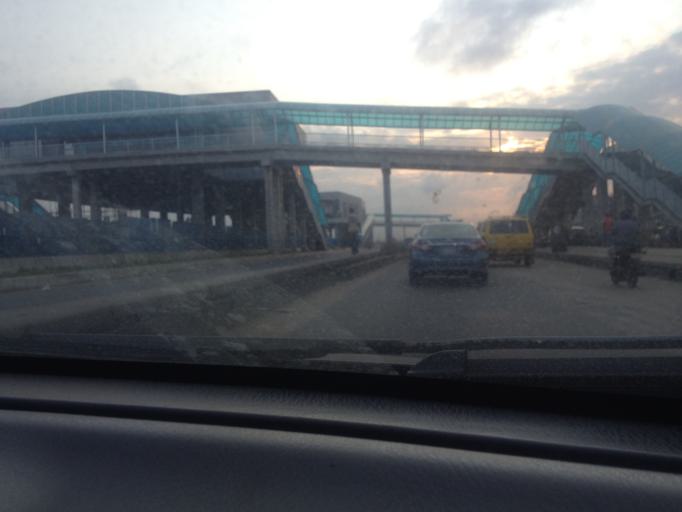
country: NG
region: Lagos
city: Ajegunle
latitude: 6.4602
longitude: 3.3130
